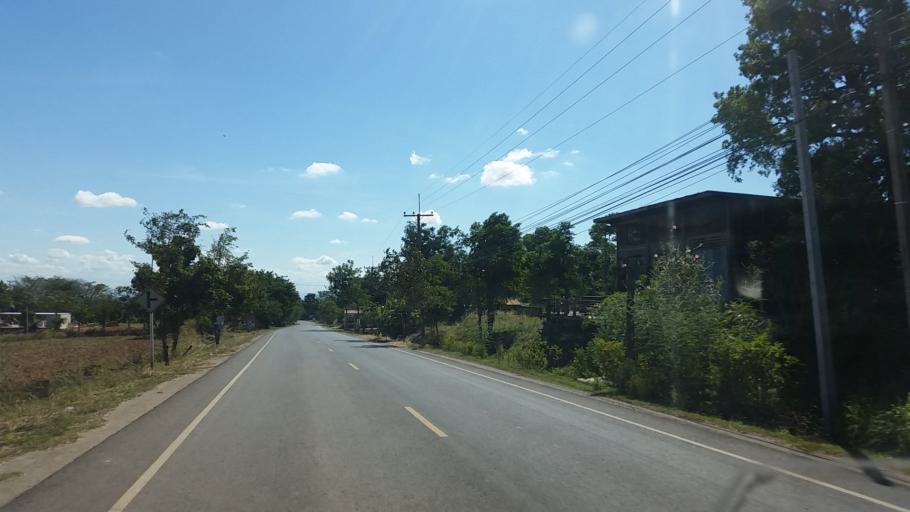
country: TH
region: Chaiyaphum
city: Thep Sathit
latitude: 15.5967
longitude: 101.4056
